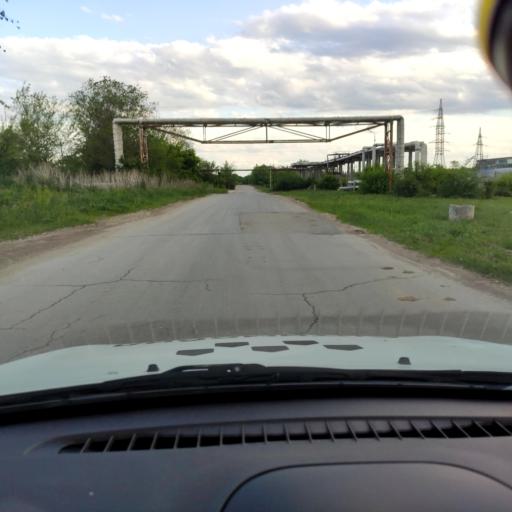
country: RU
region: Samara
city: Podstepki
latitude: 53.5810
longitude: 49.2289
